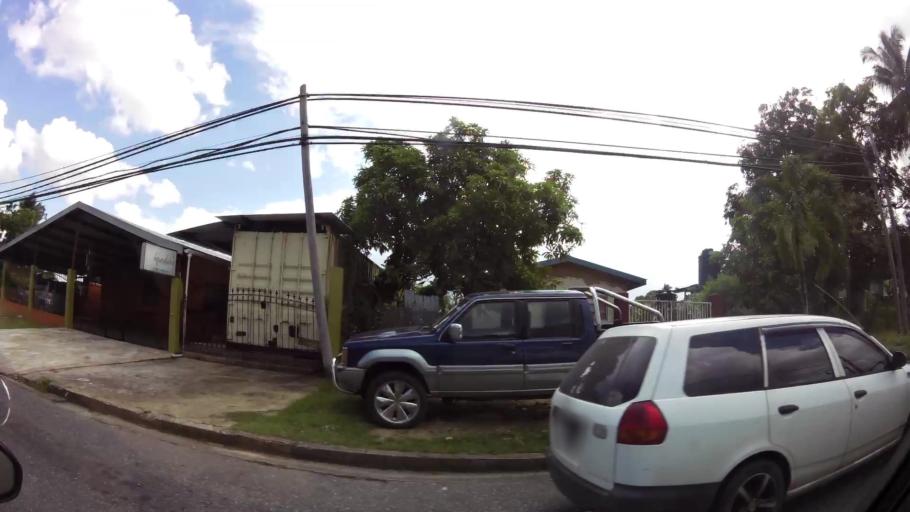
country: TT
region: City of San Fernando
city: Mon Repos
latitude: 10.2677
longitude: -61.4548
